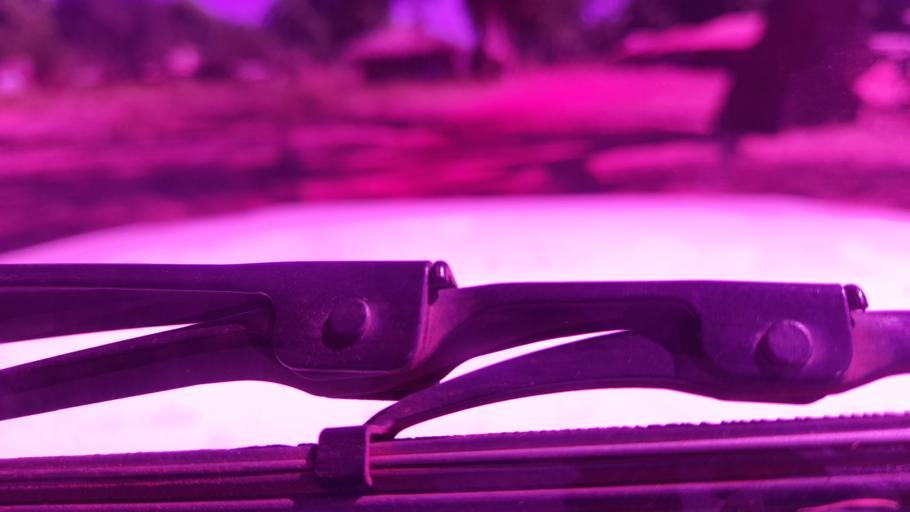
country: GW
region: Oio
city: Bissora
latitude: 12.3914
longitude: -15.6244
